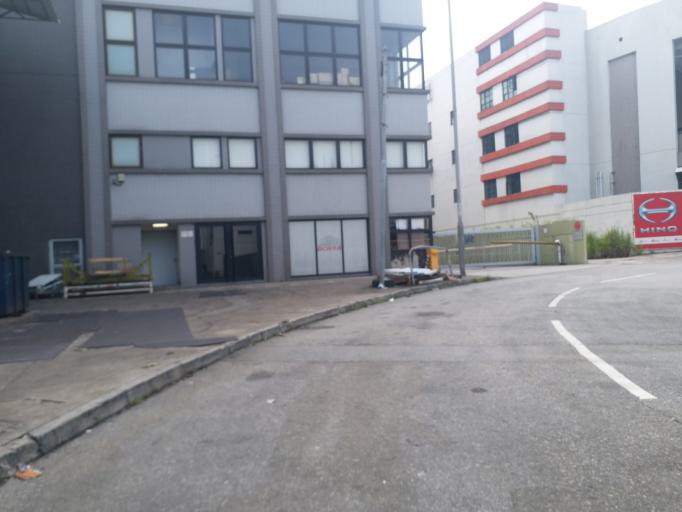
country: HK
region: Yuen Long
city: Yuen Long Kau Hui
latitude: 22.4436
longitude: 114.0028
